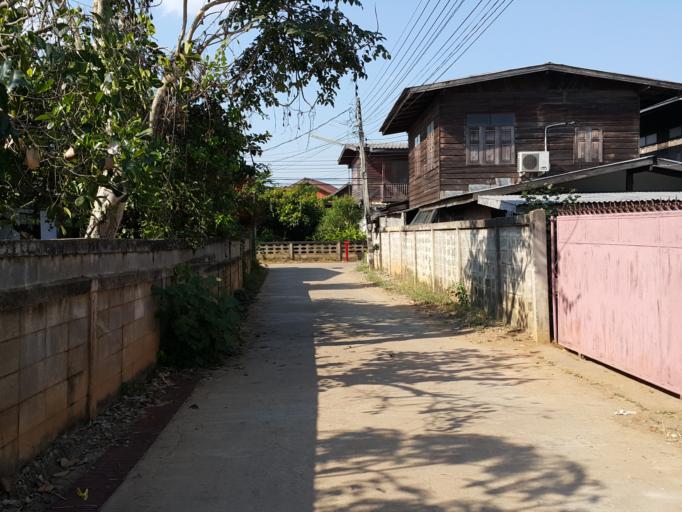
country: TH
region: Sukhothai
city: Thung Saliam
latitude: 17.3179
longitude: 99.5615
